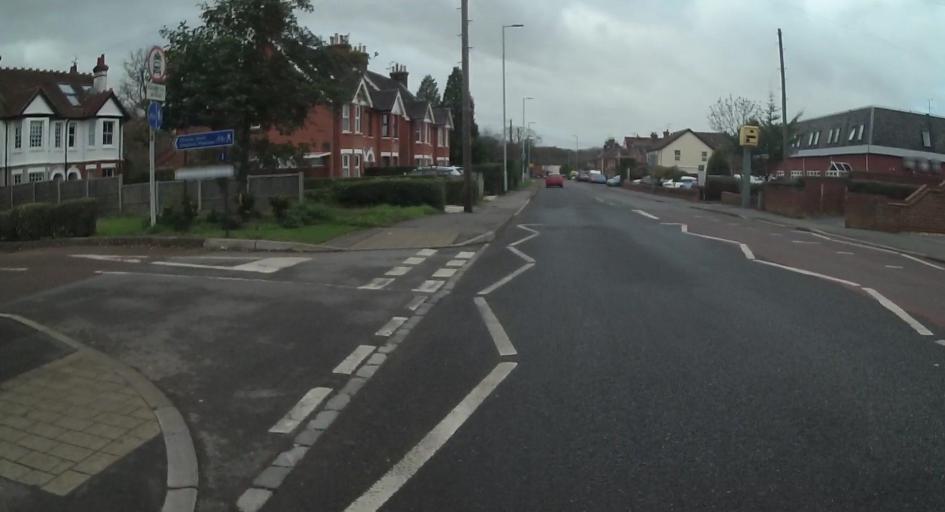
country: GB
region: England
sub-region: Bracknell Forest
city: Sandhurst
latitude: 51.3424
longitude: -0.7806
